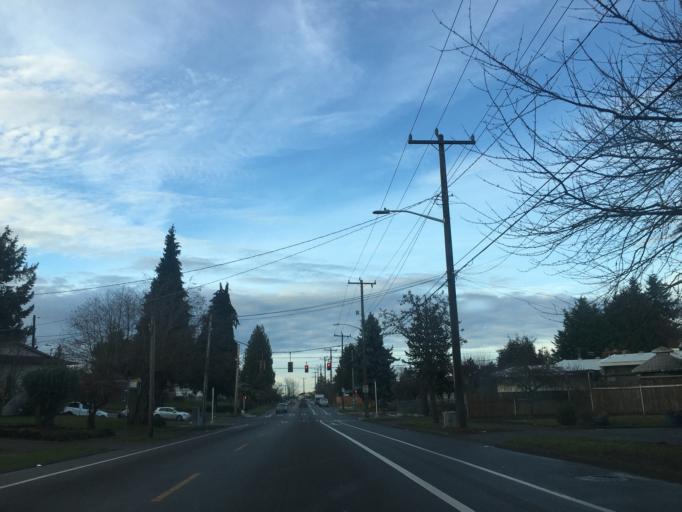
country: US
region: Washington
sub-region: King County
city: Bryn Mawr-Skyway
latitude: 47.5058
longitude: -122.2539
